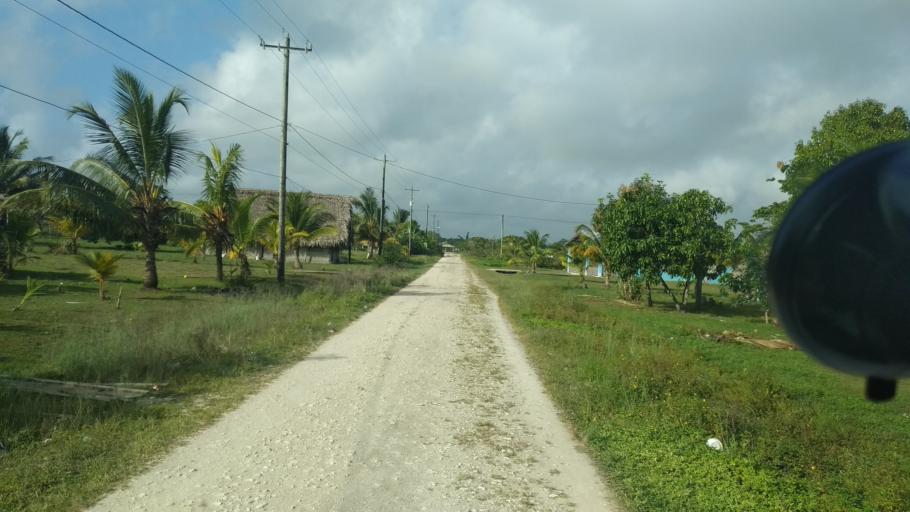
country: BZ
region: Stann Creek
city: Placencia
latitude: 16.5081
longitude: -88.5455
